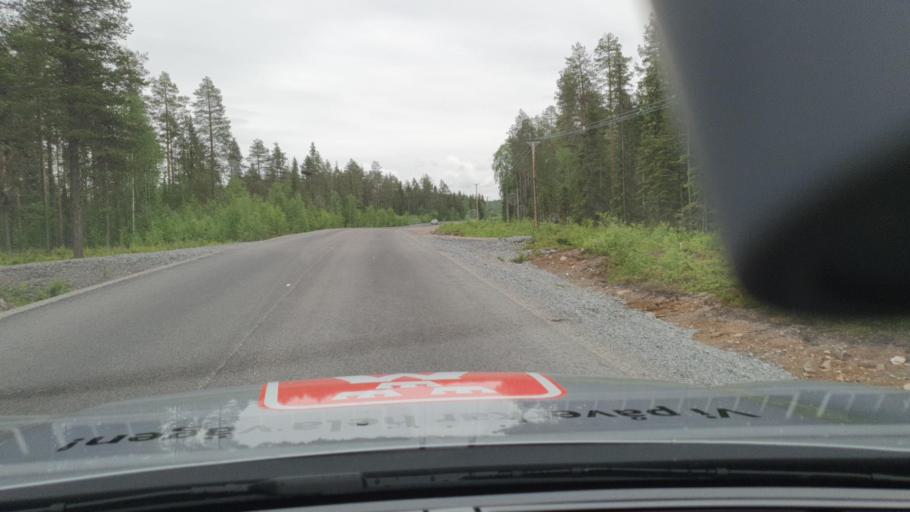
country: SE
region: Norrbotten
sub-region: Overtornea Kommun
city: OEvertornea
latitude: 66.6368
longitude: 23.2596
